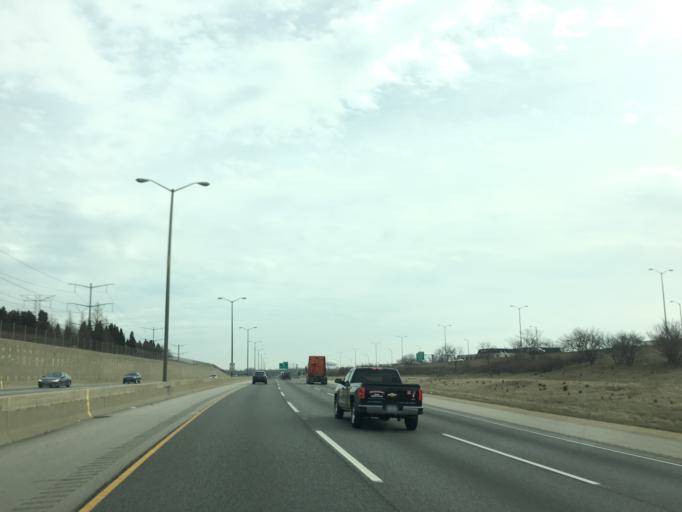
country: US
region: Illinois
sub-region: DuPage County
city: Lisle
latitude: 41.8105
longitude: -88.0463
